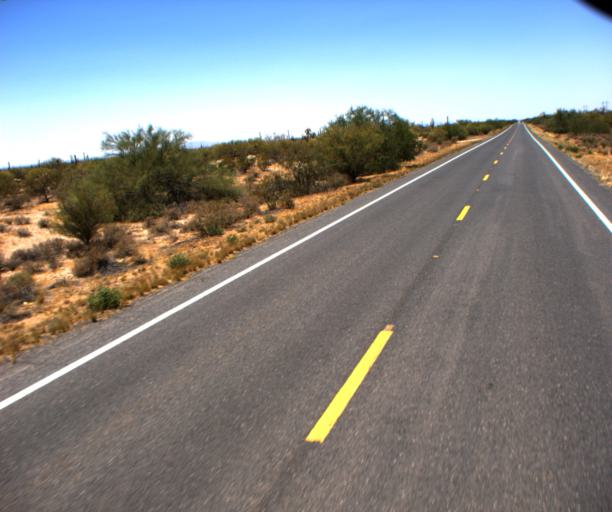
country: US
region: Arizona
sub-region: Pinal County
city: Florence
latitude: 32.8577
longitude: -111.2377
